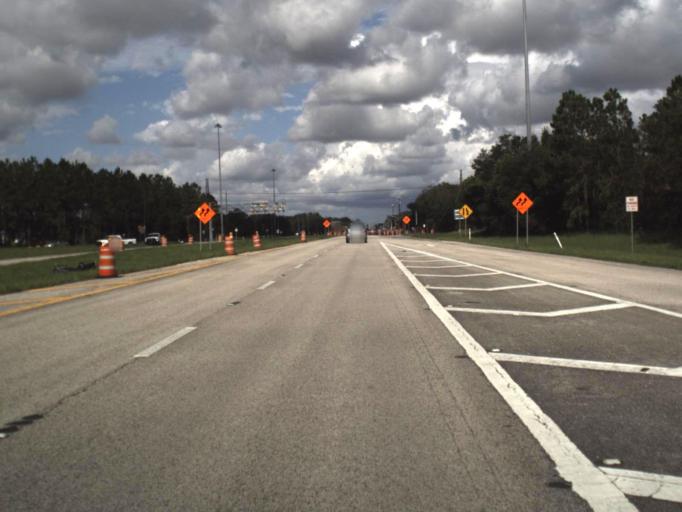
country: US
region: Florida
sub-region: Hillsborough County
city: Temple Terrace
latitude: 28.0543
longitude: -82.3565
